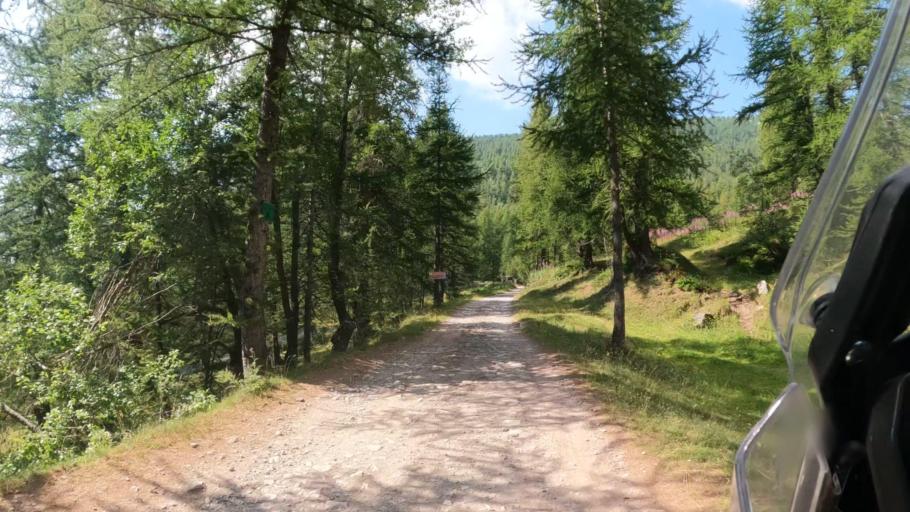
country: IT
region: Piedmont
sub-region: Provincia di Cuneo
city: Briga Alta
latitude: 44.1109
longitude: 7.7037
